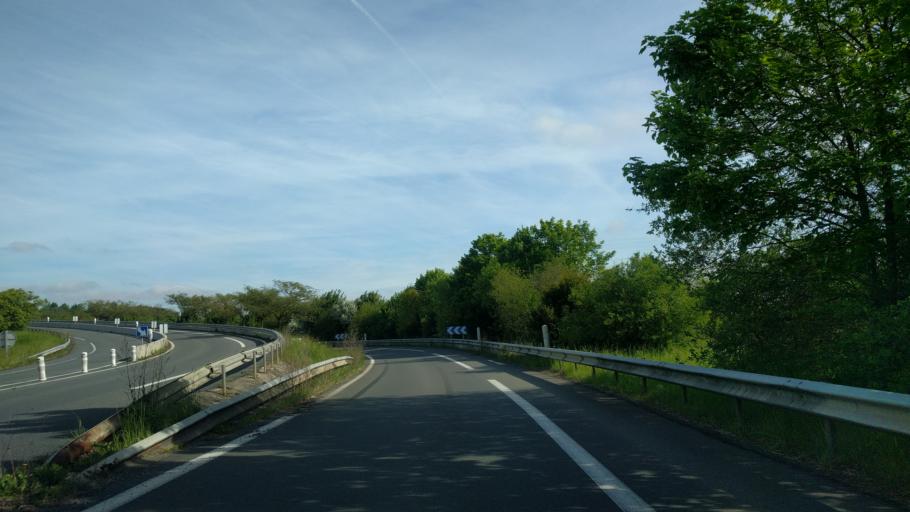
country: FR
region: Picardie
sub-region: Departement de la Somme
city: Peronne
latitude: 49.9678
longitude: 2.8634
